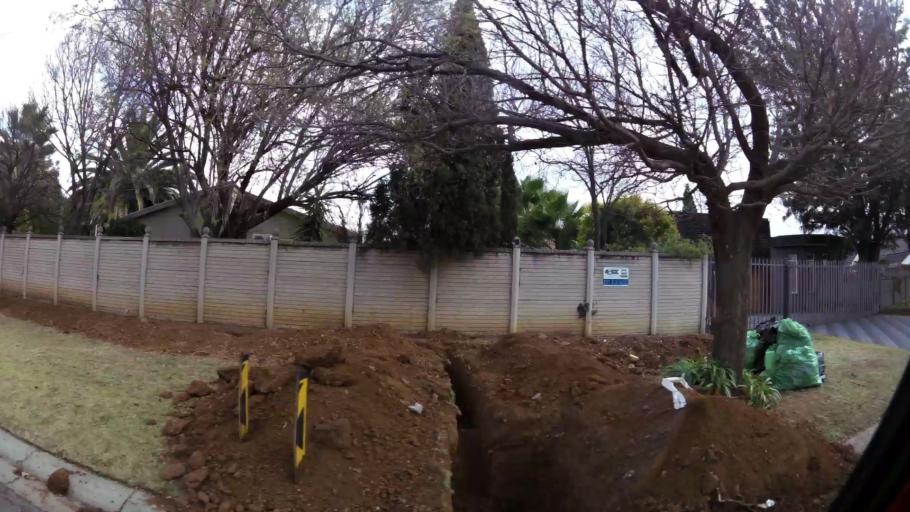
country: ZA
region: Gauteng
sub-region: Sedibeng District Municipality
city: Vanderbijlpark
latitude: -26.7258
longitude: 27.8477
